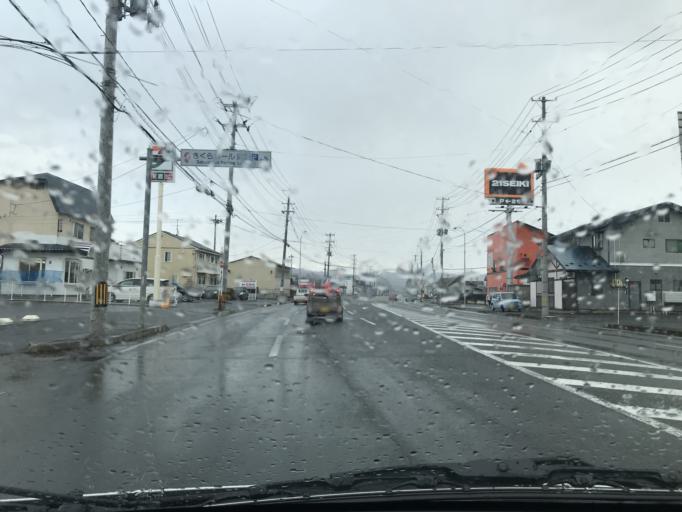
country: JP
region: Iwate
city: Kitakami
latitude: 39.2996
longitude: 141.1086
